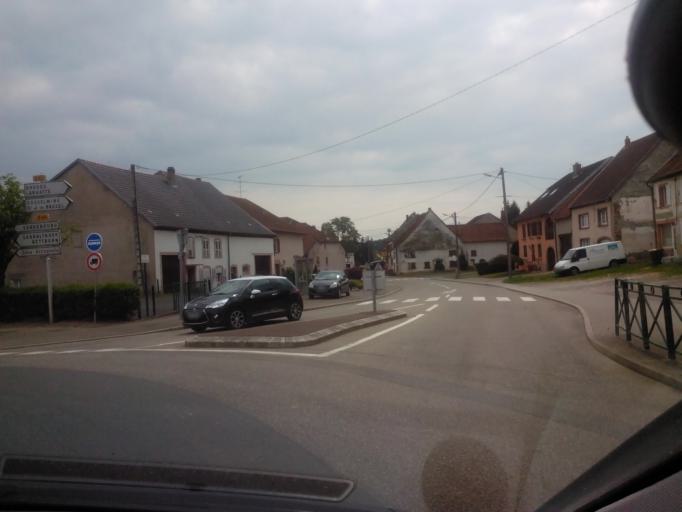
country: FR
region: Lorraine
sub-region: Departement de la Moselle
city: Sarrebourg
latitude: 48.8166
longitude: 7.0064
